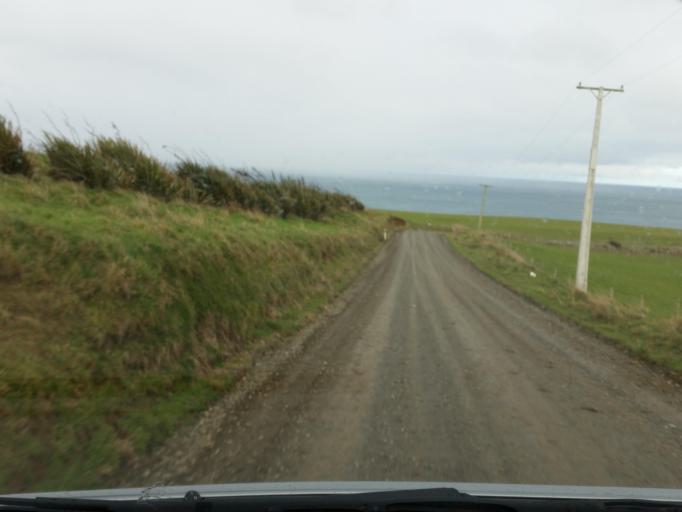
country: NZ
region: Otago
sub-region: Clutha District
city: Papatowai
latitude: -46.6676
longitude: 169.0066
